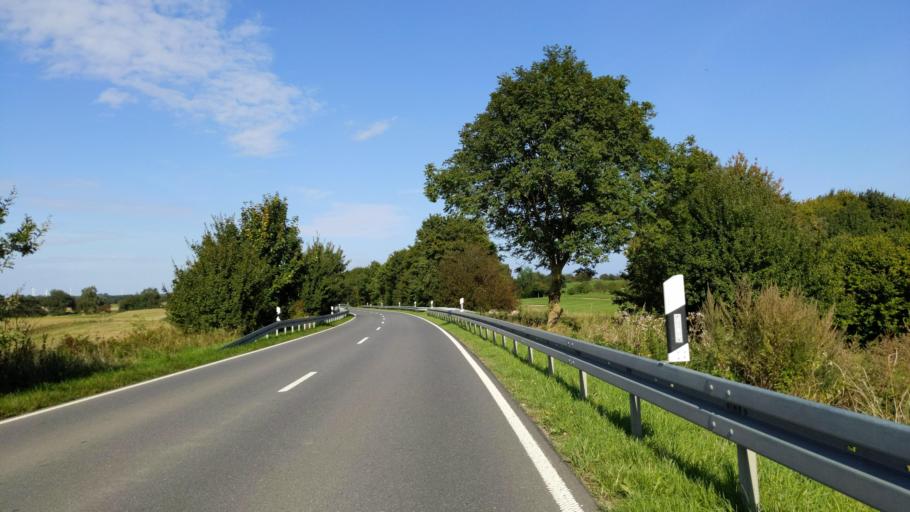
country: DE
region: Schleswig-Holstein
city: Stockelsdorf
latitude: 53.9548
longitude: 10.6298
